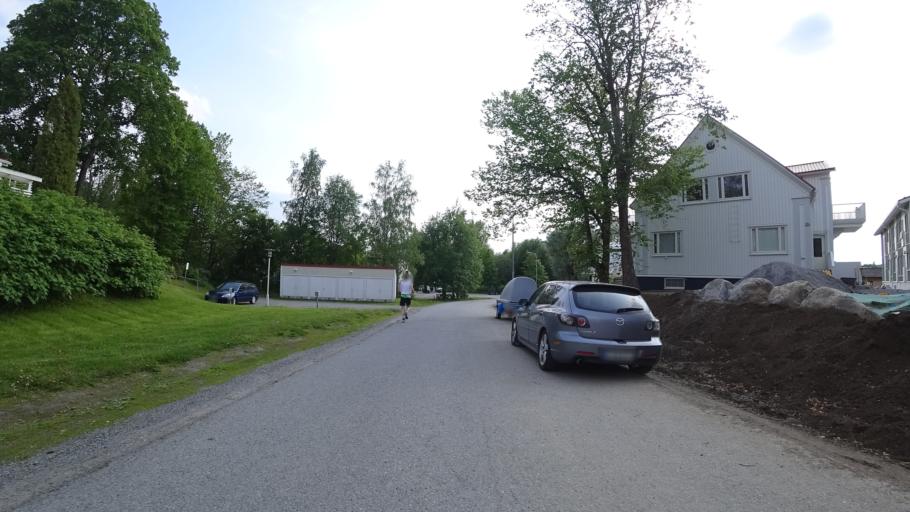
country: FI
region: Pirkanmaa
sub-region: Tampere
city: Pirkkala
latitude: 61.5036
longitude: 23.6912
